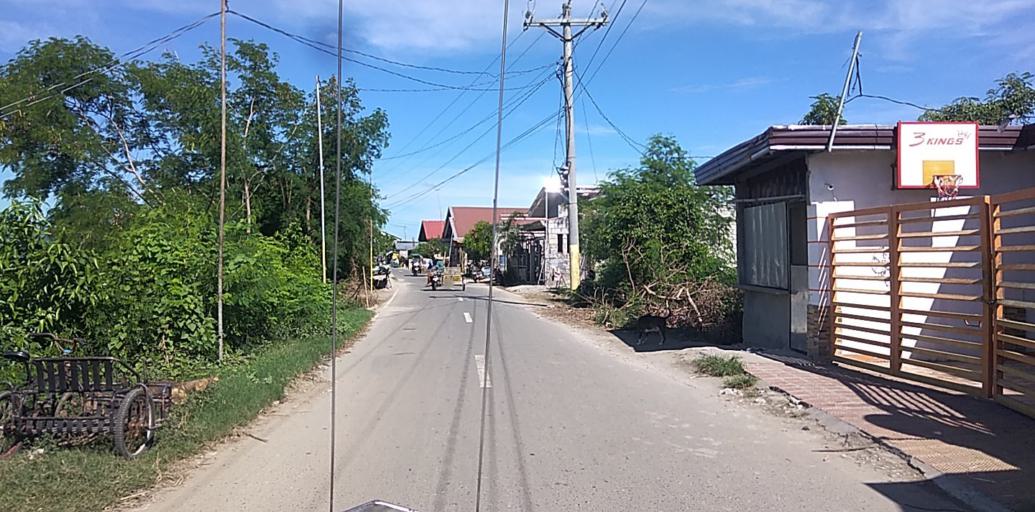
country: PH
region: Central Luzon
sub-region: Province of Pampanga
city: Candaba
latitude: 15.1097
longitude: 120.8167
